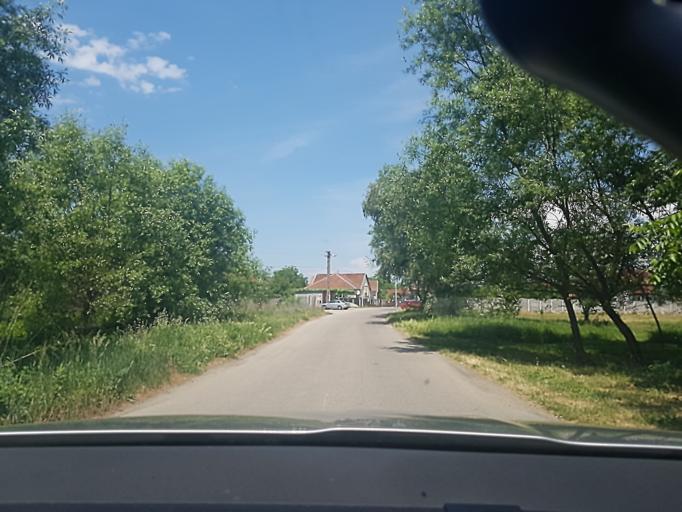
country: RO
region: Hunedoara
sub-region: Comuna Calan
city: Calan
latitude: 45.7386
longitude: 23.0088
